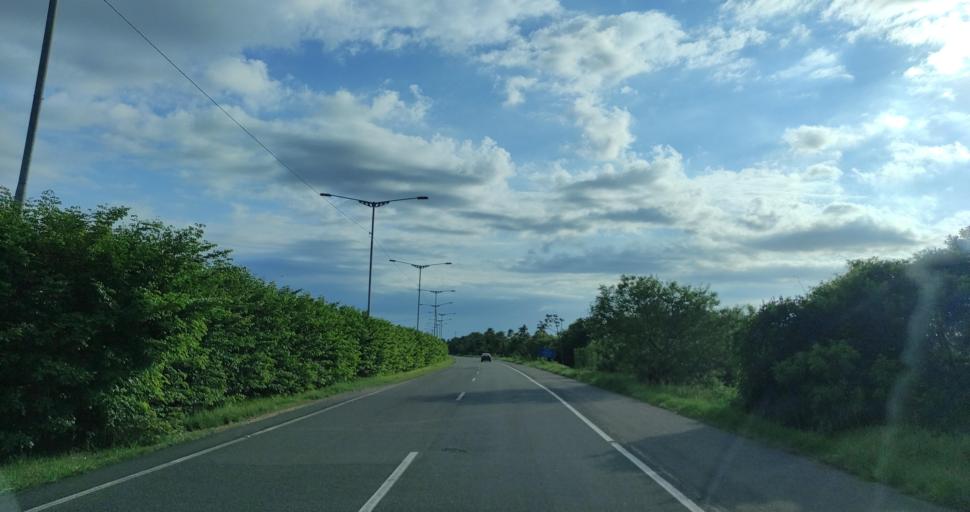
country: BR
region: Santa Catarina
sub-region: Penha
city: Penha
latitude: -26.8025
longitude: -48.6308
